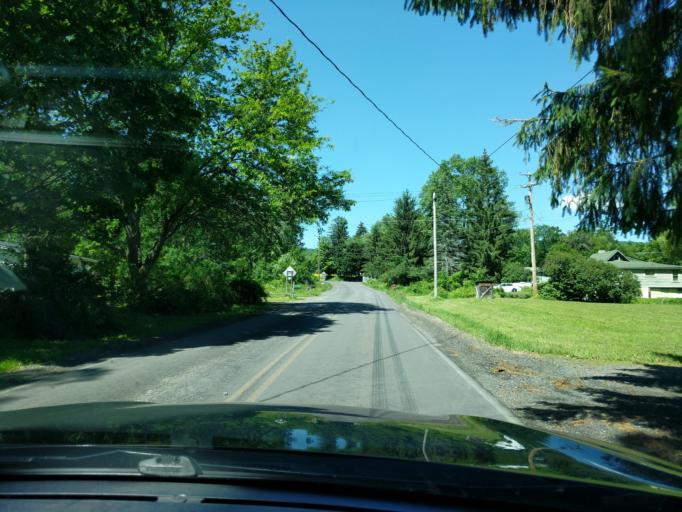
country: US
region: New York
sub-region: Tompkins County
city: East Ithaca
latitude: 42.3706
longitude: -76.4019
